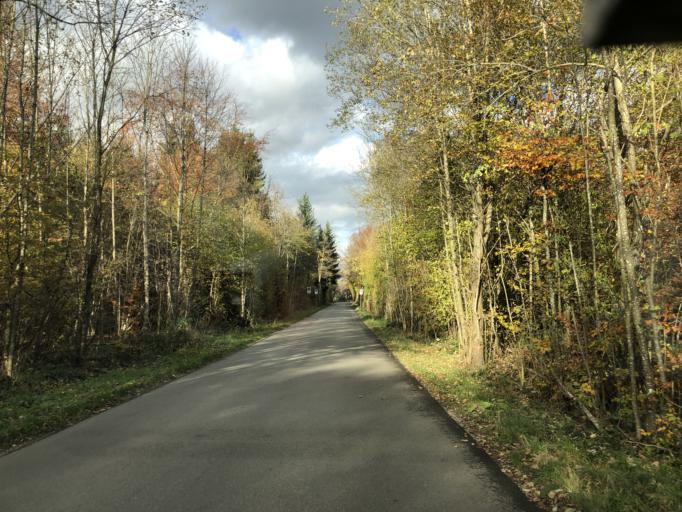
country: CH
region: Aargau
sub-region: Bezirk Baden
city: Obersiggenthal
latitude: 47.4718
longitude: 8.2786
